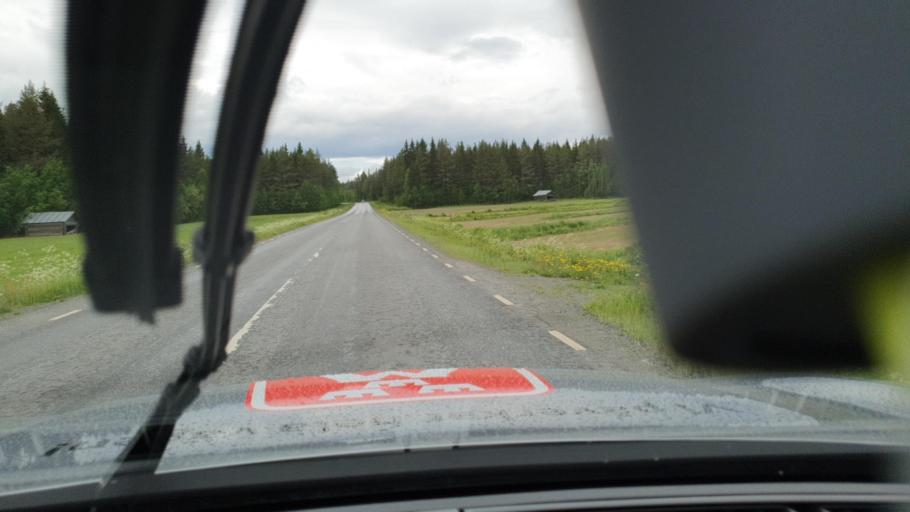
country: SE
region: Norrbotten
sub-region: Lulea Kommun
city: Ranea
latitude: 65.7849
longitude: 22.1611
